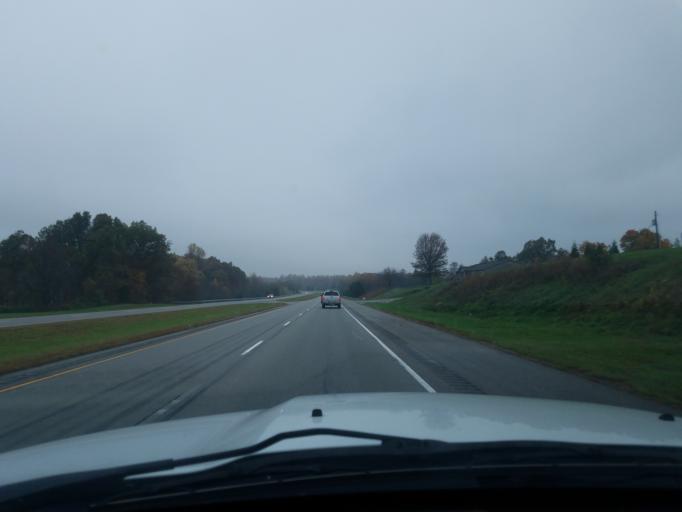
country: US
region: Kentucky
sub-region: Hardin County
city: Elizabethtown
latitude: 37.6495
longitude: -85.8375
